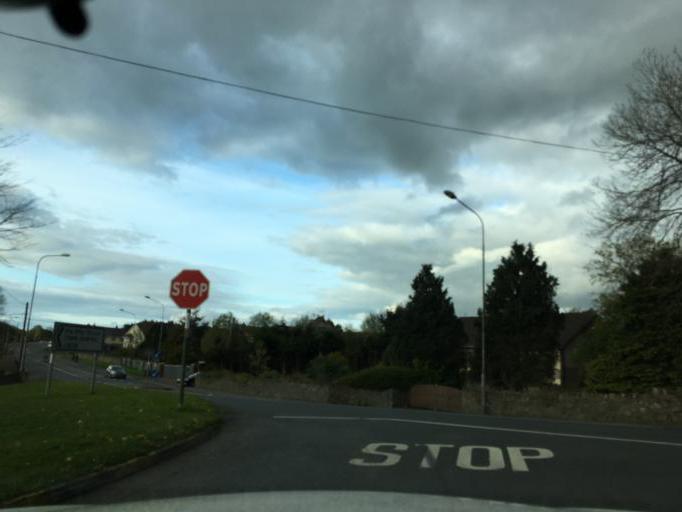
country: IE
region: Leinster
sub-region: Loch Garman
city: New Ross
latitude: 52.4027
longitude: -6.9370
